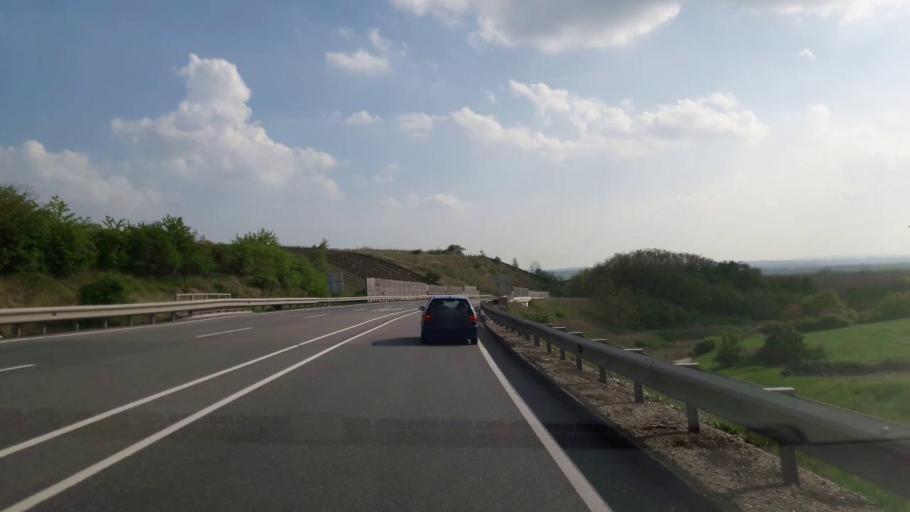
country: AT
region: Lower Austria
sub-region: Politischer Bezirk Hollabrunn
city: Haugsdorf
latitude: 48.7351
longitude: 16.0581
